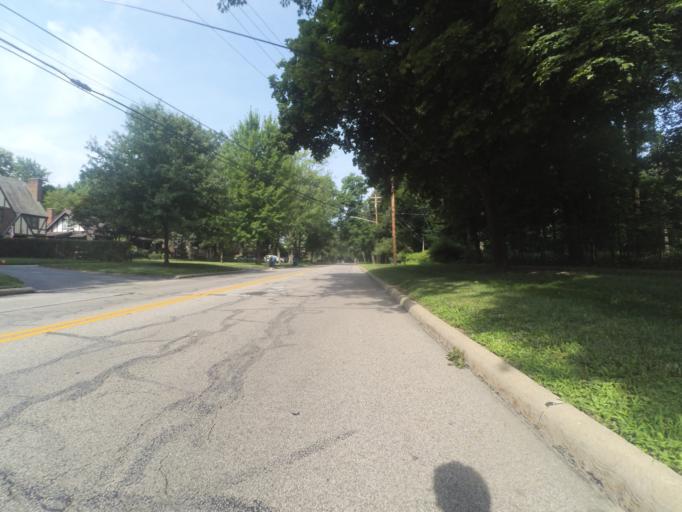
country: US
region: Ohio
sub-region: Cuyahoga County
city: Bratenahl
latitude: 41.5485
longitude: -81.6113
